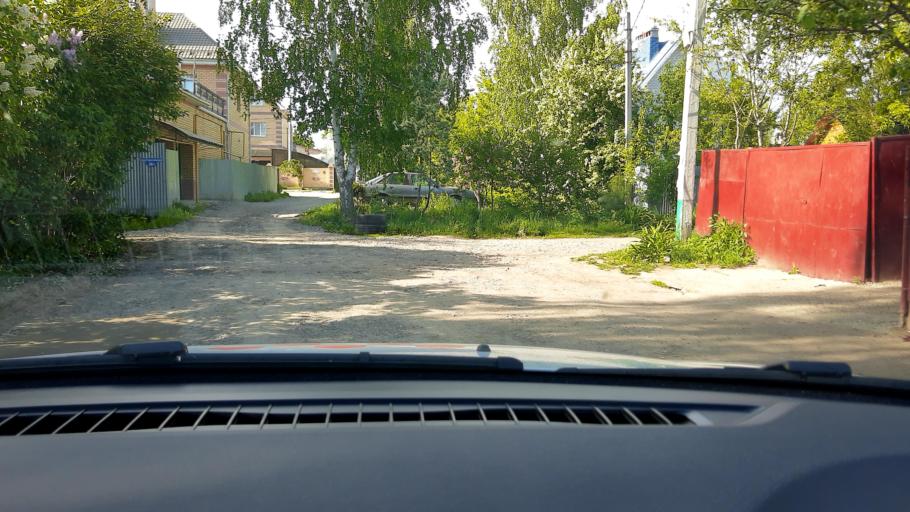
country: RU
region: Nizjnij Novgorod
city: Burevestnik
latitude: 56.2030
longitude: 43.7889
